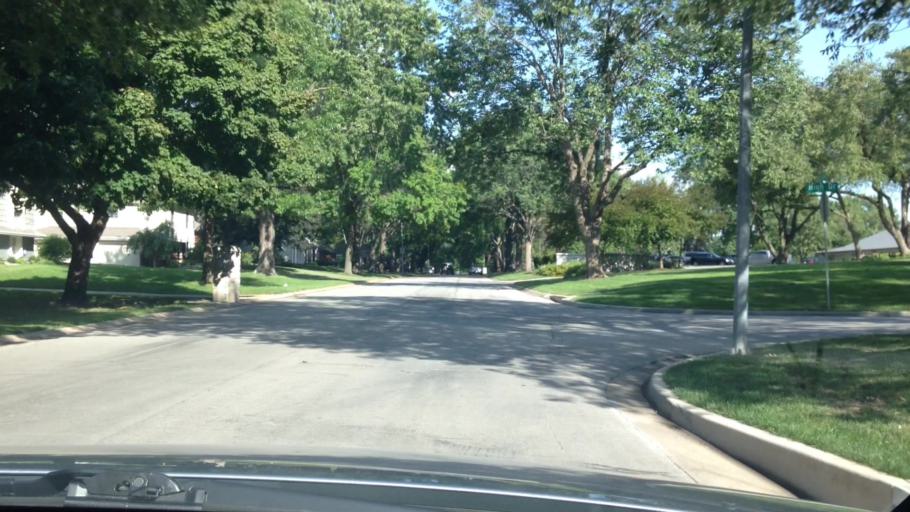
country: US
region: Kansas
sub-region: Johnson County
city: Leawood
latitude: 38.8979
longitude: -94.6176
